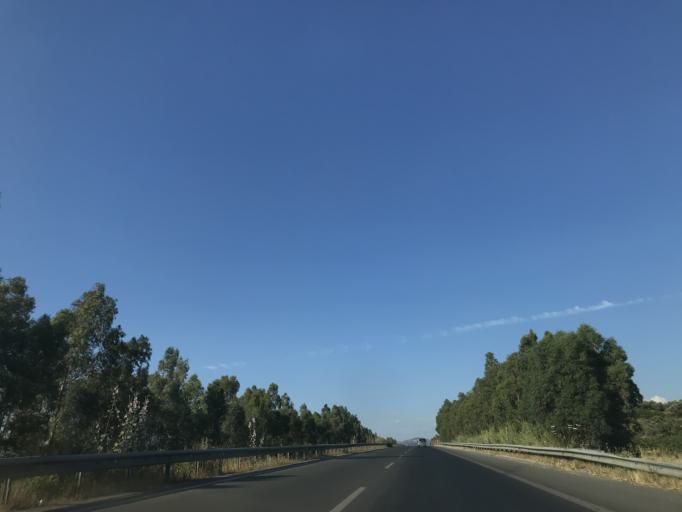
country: TR
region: Aydin
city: Germencik
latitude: 37.8505
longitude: 27.5482
